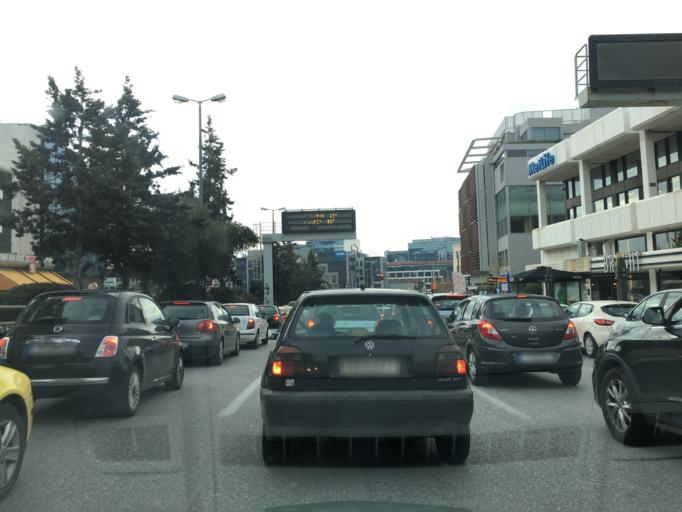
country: GR
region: Attica
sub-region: Nomarchia Athinas
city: Marousi
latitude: 38.0475
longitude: 23.8077
